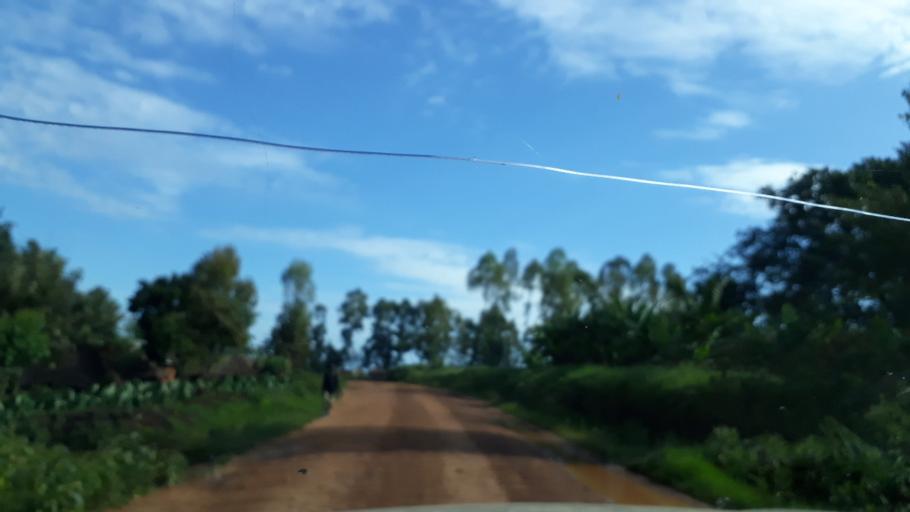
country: UG
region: Northern Region
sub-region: Zombo District
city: Paidha
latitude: 2.3330
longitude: 31.0274
